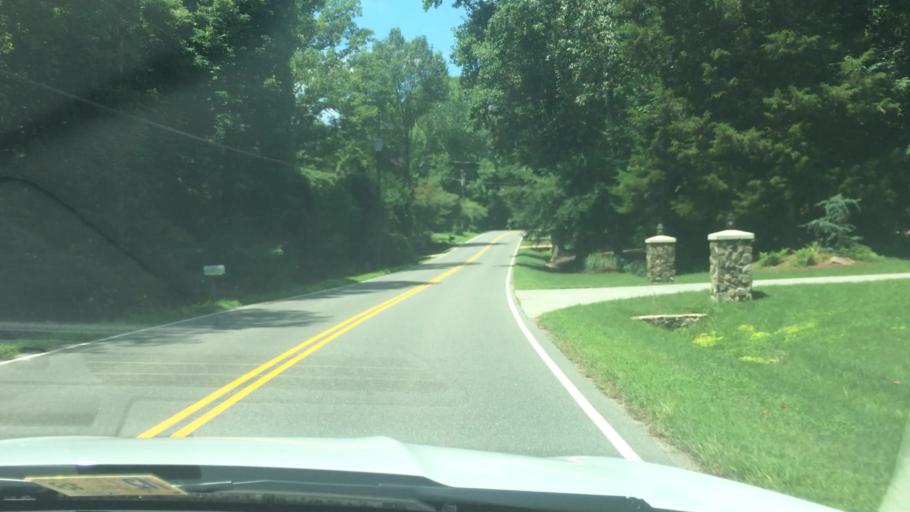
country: US
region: Virginia
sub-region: James City County
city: Williamsburg
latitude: 37.2794
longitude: -76.7976
